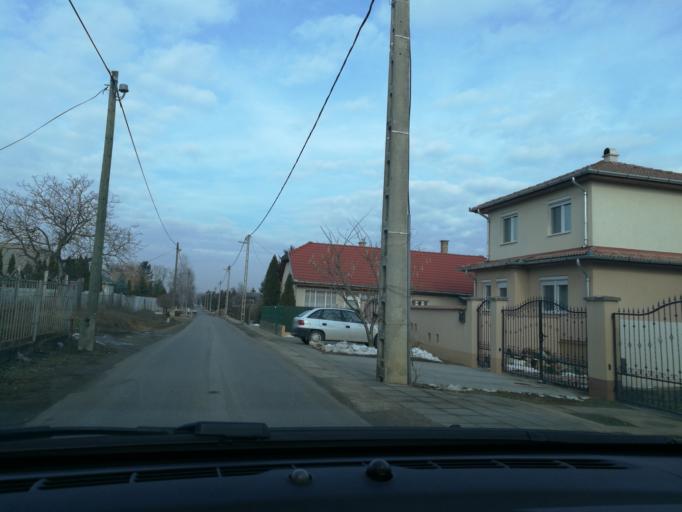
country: HU
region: Szabolcs-Szatmar-Bereg
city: Nyiregyhaza
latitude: 47.9378
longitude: 21.7371
